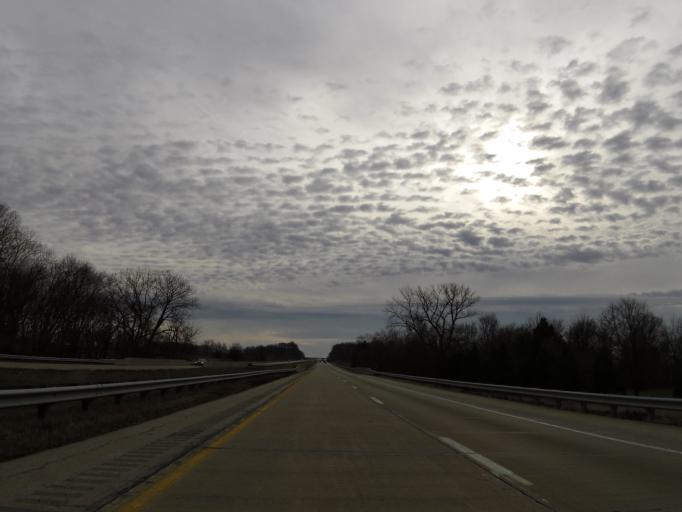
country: US
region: Indiana
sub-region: Hendricks County
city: Pittsboro
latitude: 39.9303
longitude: -86.5951
